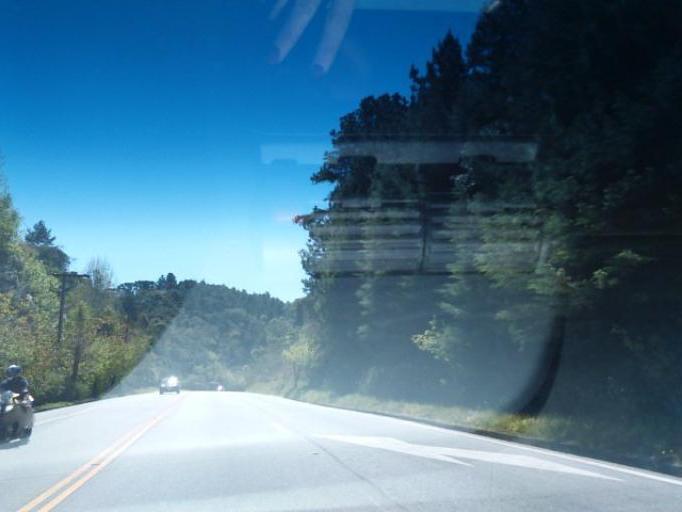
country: BR
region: Sao Paulo
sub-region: Campos Do Jordao
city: Campos do Jordao
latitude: -22.7687
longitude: -45.6142
